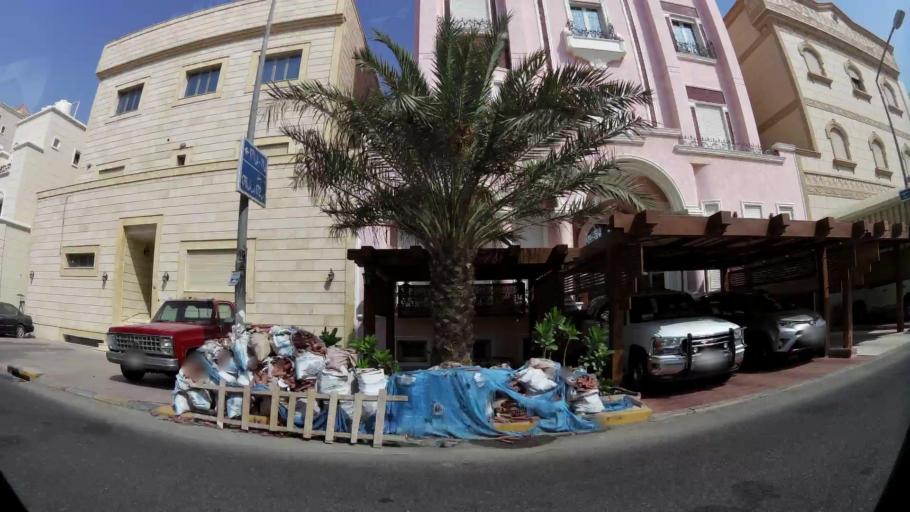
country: KW
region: Muhafazat al Jahra'
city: Al Jahra'
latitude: 29.3220
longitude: 47.7383
